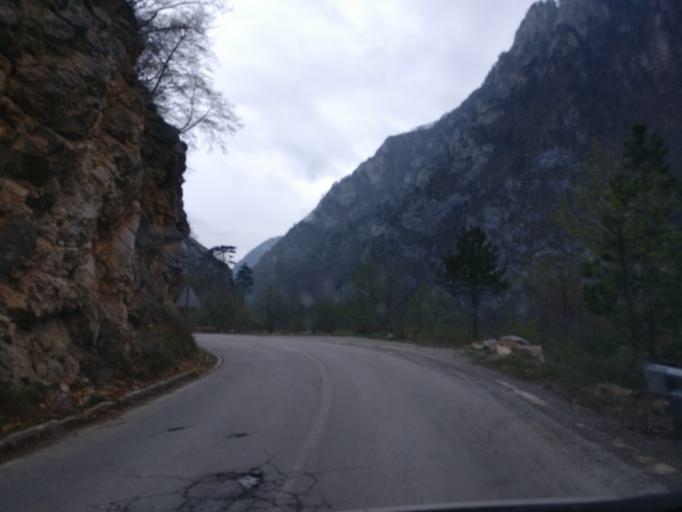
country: ME
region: Opstina Pluzine
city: Pluzine
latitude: 43.2459
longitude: 18.8344
